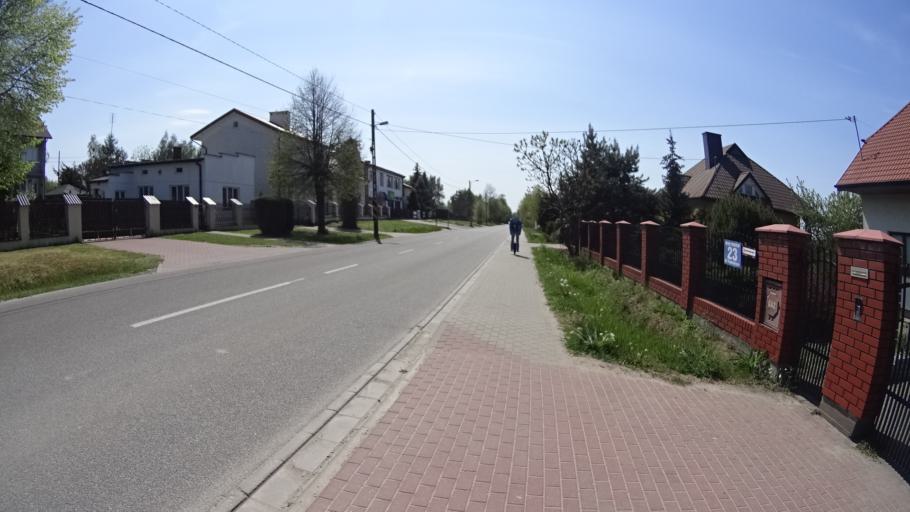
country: PL
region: Masovian Voivodeship
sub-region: Powiat warszawski zachodni
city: Jozefow
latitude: 52.2642
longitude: 20.7023
